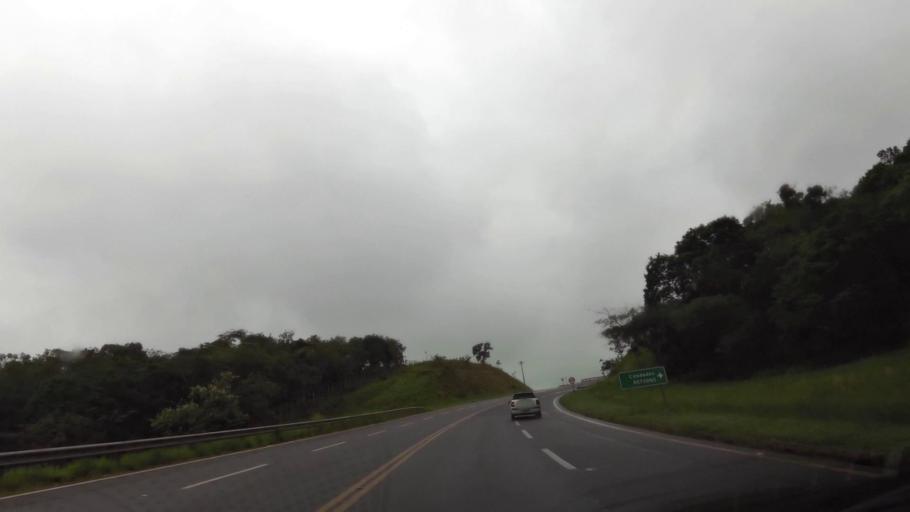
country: BR
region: Espirito Santo
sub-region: Guarapari
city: Guarapari
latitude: -20.7332
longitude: -40.5566
